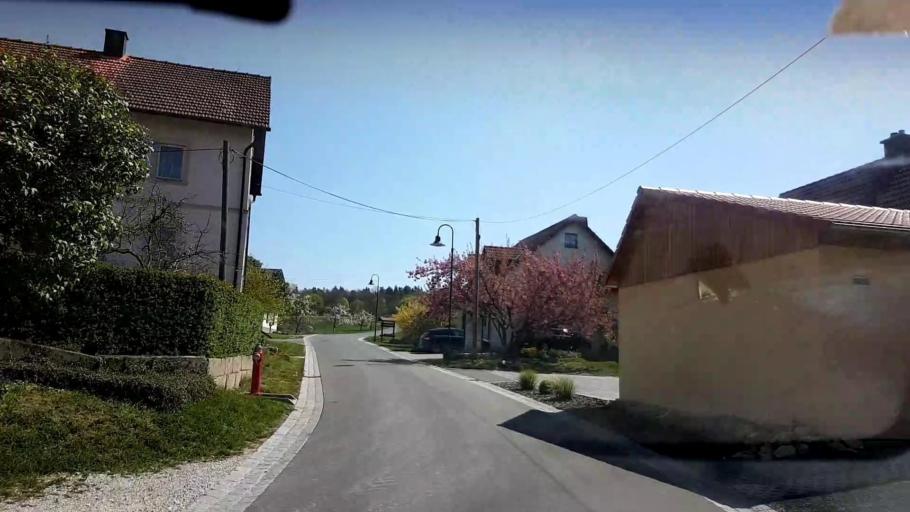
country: DE
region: Bavaria
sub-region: Upper Franconia
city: Zapfendorf
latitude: 50.0001
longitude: 10.9685
